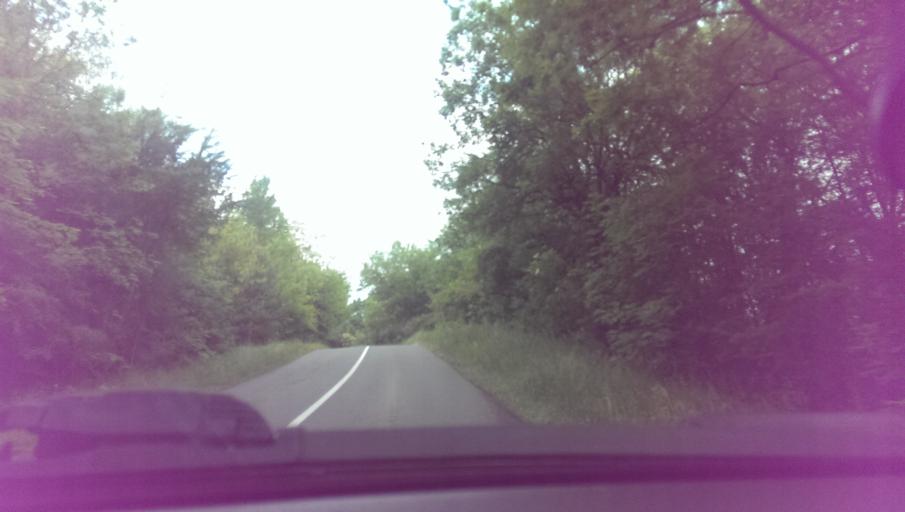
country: CZ
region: Zlin
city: Kvasice
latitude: 49.2321
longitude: 17.4865
